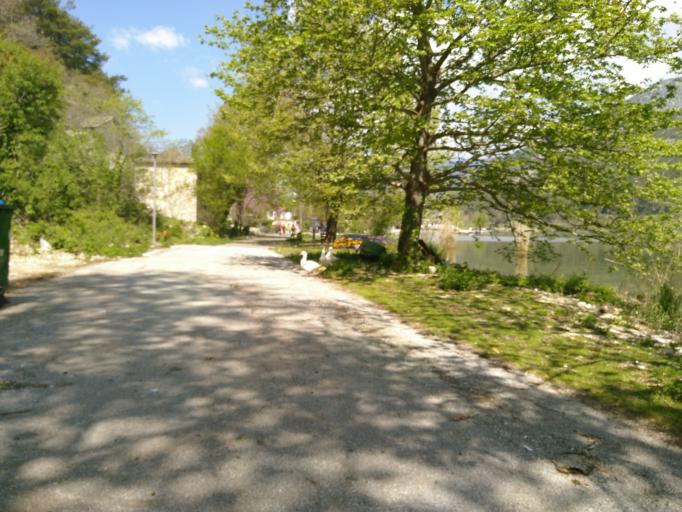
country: GR
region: Epirus
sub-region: Nomos Ioanninon
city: Ioannina
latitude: 39.6784
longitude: 20.8770
